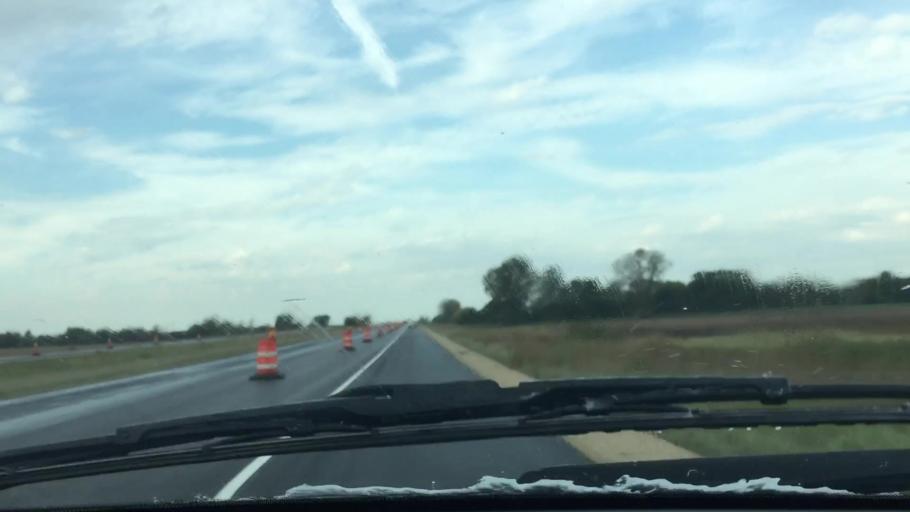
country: US
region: Illinois
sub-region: Whiteside County
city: Erie
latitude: 41.7096
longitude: -90.0211
